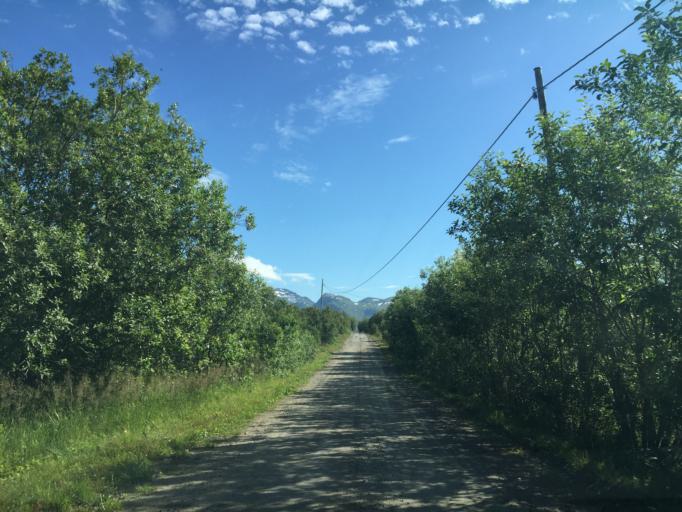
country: NO
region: Nordland
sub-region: Vagan
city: Kabelvag
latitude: 68.3543
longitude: 14.4491
